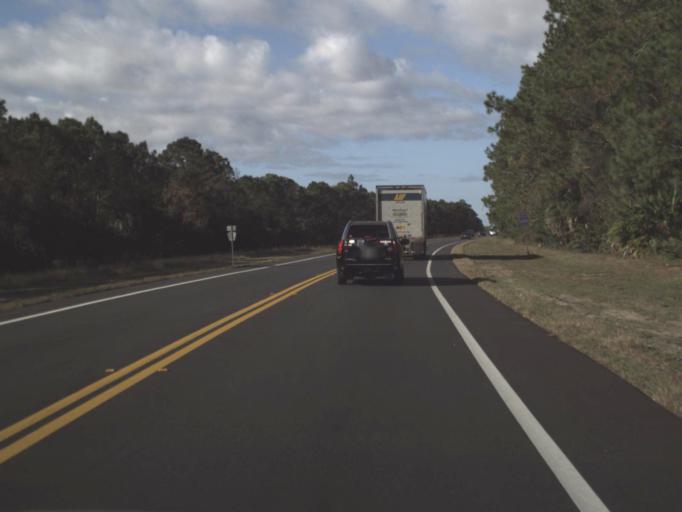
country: US
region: Florida
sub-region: Volusia County
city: South Daytona
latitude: 29.1410
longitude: -81.0576
